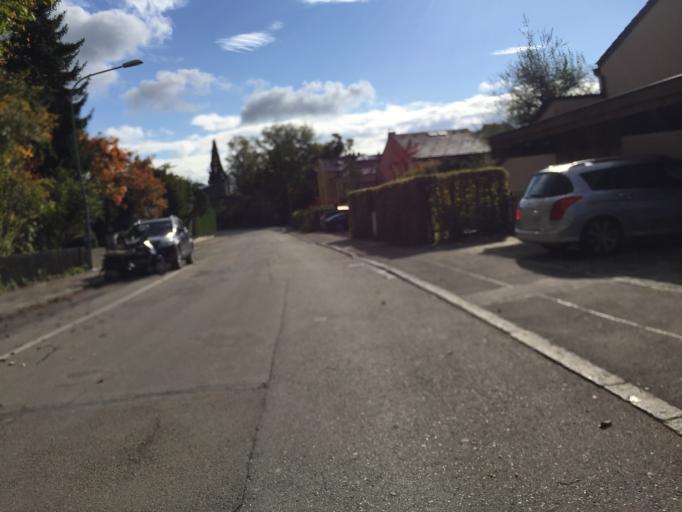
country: CH
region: Bern
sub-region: Bern-Mittelland District
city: Muri
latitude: 46.9262
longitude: 7.4742
